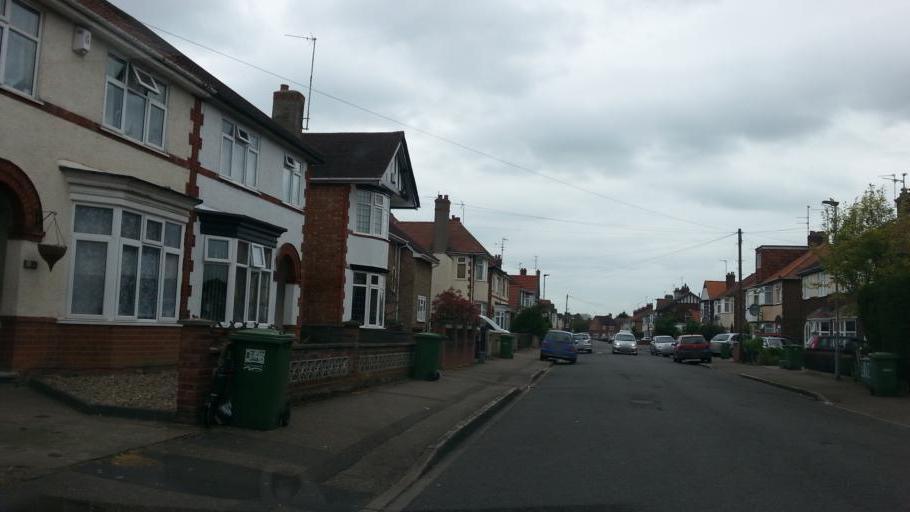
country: GB
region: England
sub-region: Peterborough
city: Peterborough
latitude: 52.5916
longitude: -0.2427
